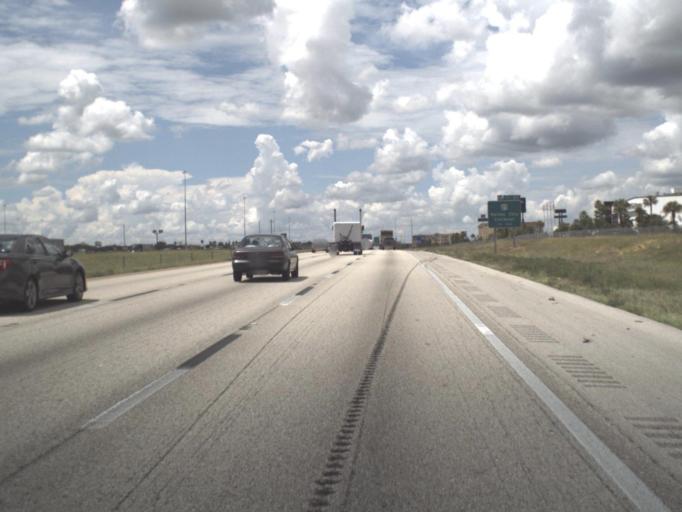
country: US
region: Florida
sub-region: Polk County
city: Loughman
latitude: 28.2387
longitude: -81.6420
